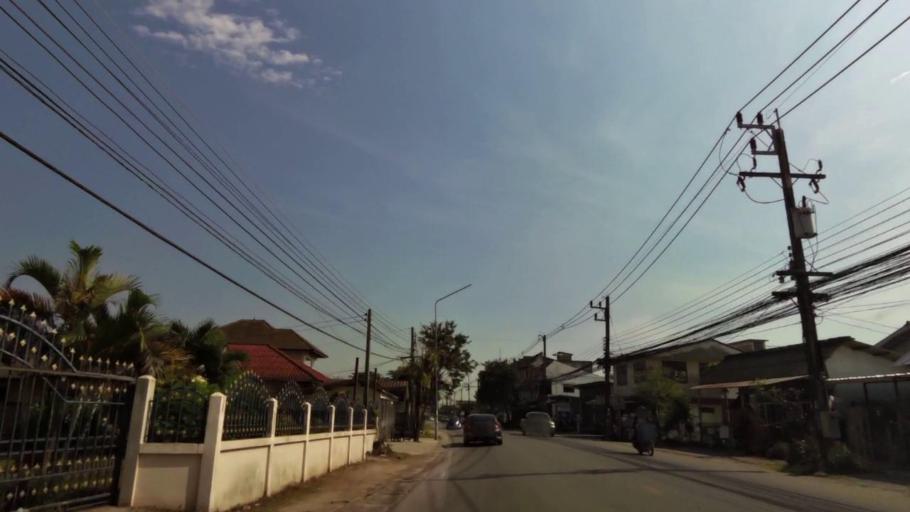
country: TH
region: Chiang Rai
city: Chiang Rai
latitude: 19.9252
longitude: 99.8384
